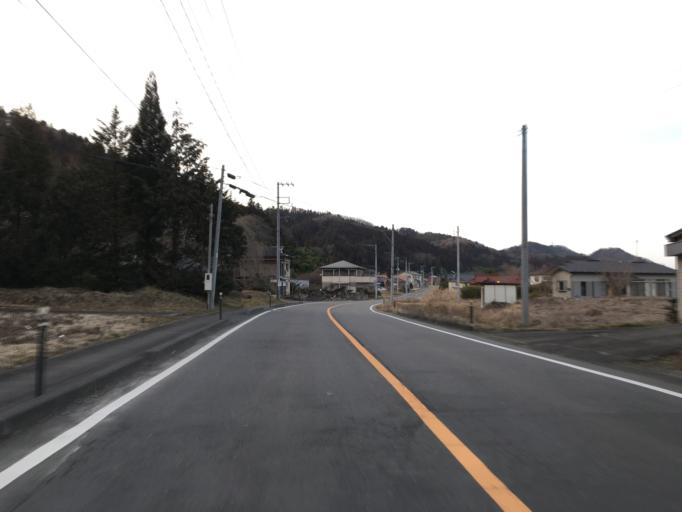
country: JP
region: Ibaraki
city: Daigo
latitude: 36.8965
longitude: 140.4097
